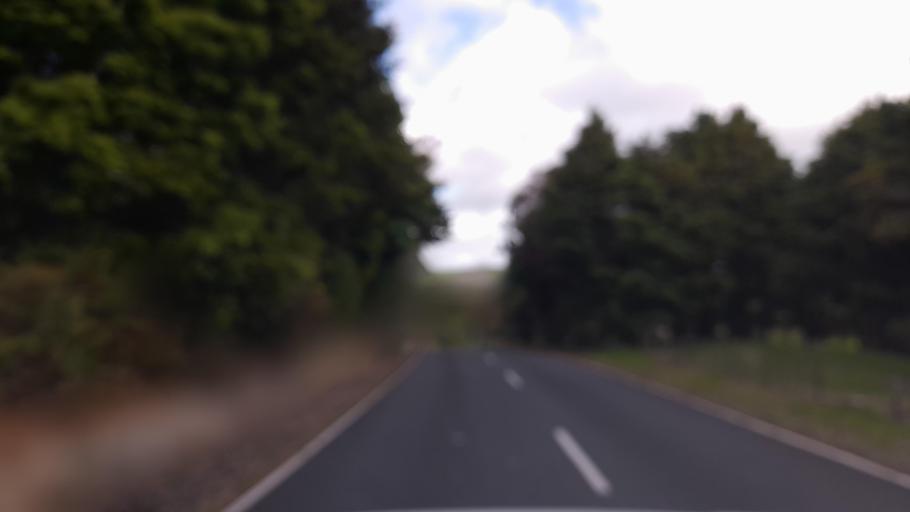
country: NZ
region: Northland
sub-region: Whangarei
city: Maungatapere
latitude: -35.7705
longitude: 174.2448
